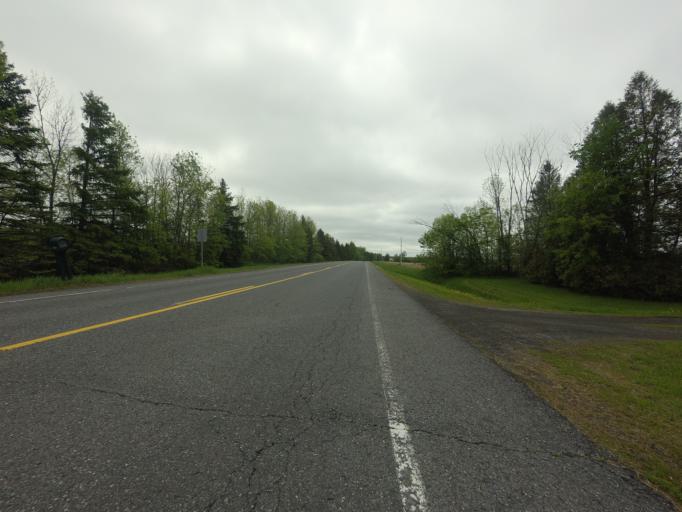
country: CA
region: Ontario
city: Casselman
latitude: 45.0561
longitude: -75.2021
